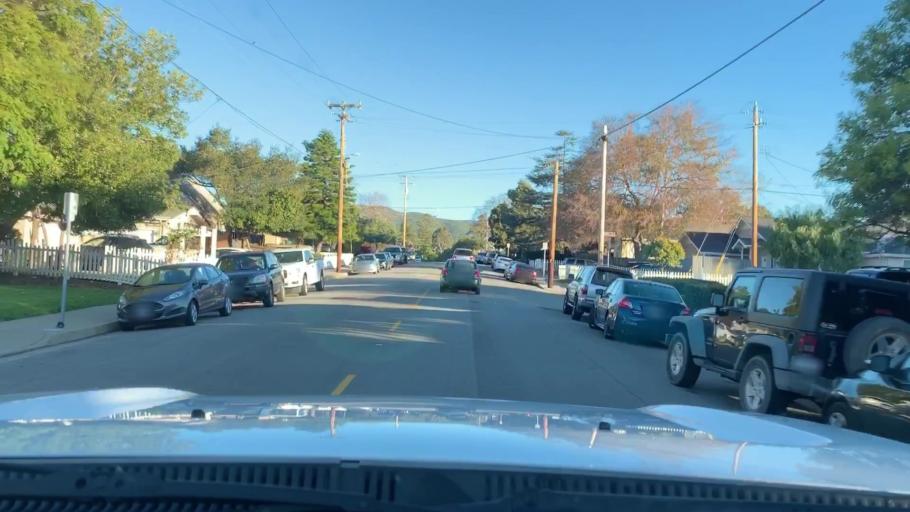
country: US
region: California
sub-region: San Luis Obispo County
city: San Luis Obispo
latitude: 35.2938
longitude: -120.6614
